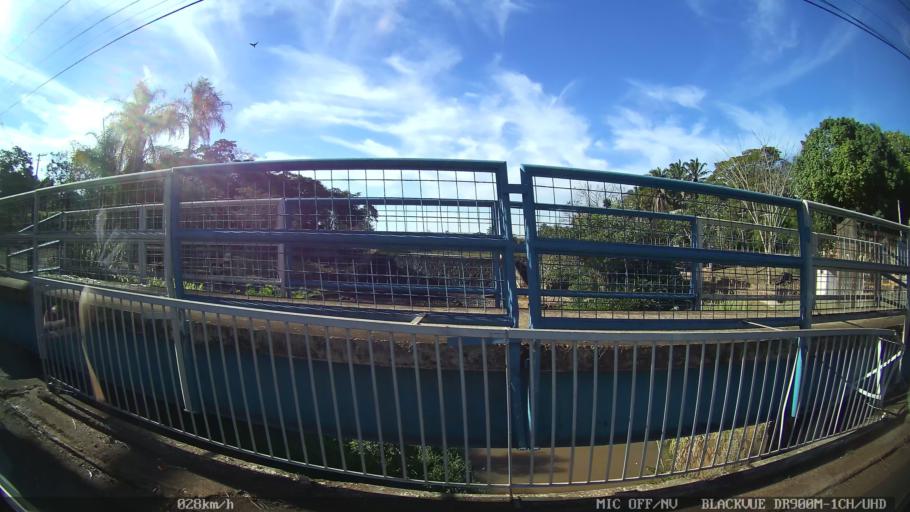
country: BR
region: Sao Paulo
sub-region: Araraquara
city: Araraquara
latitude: -21.7577
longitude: -48.1793
